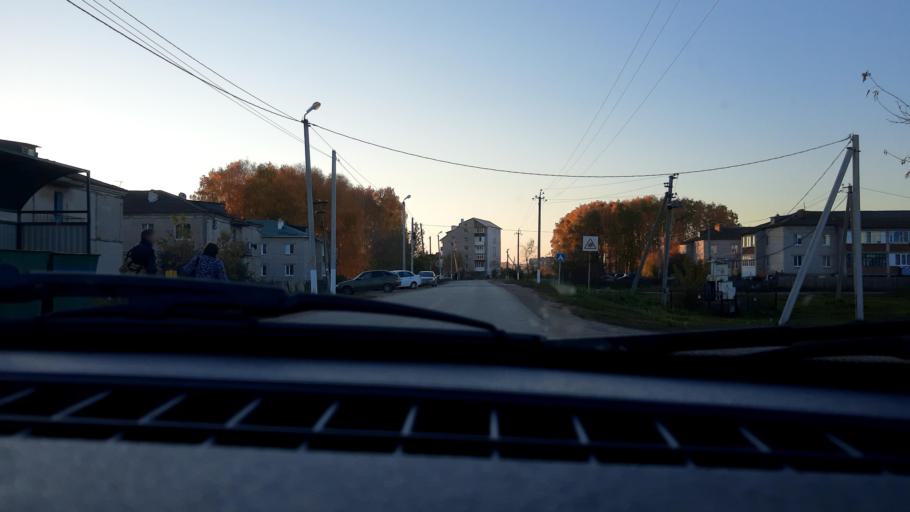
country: RU
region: Bashkortostan
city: Mikhaylovka
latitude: 54.7816
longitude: 55.8390
